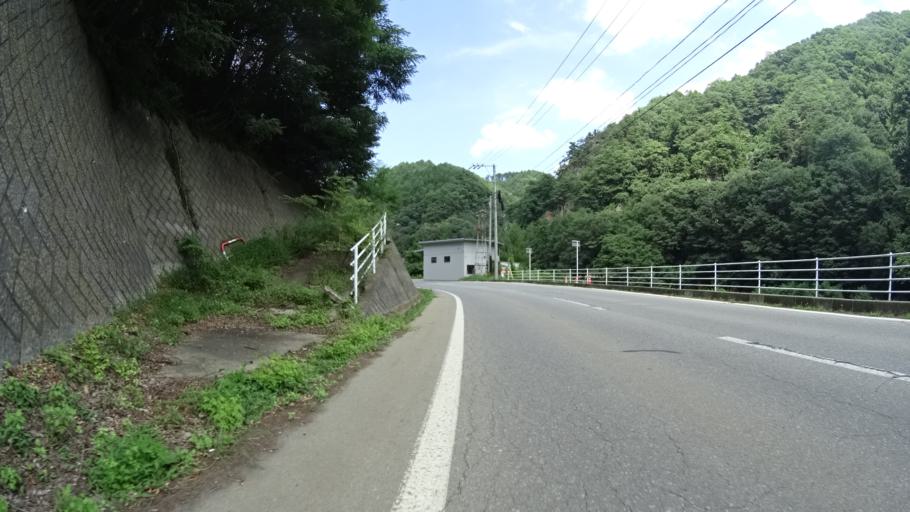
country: JP
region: Nagano
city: Saku
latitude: 36.0642
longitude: 138.5029
